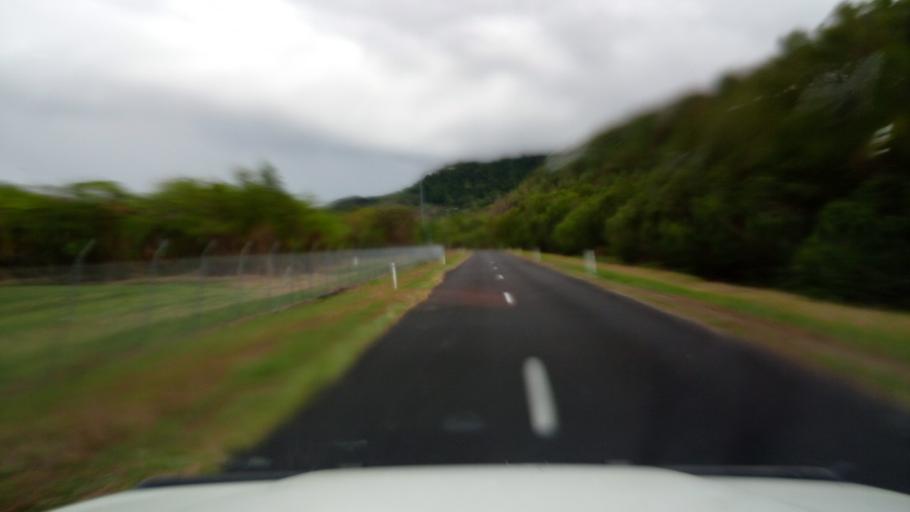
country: AU
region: Queensland
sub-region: Cairns
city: Redlynch
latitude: -16.8747
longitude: 145.7443
